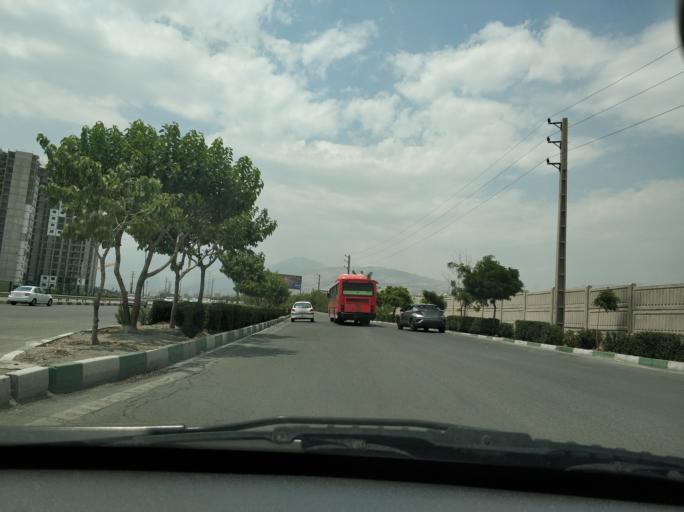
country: IR
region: Tehran
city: Tajrish
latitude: 35.7566
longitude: 51.5760
